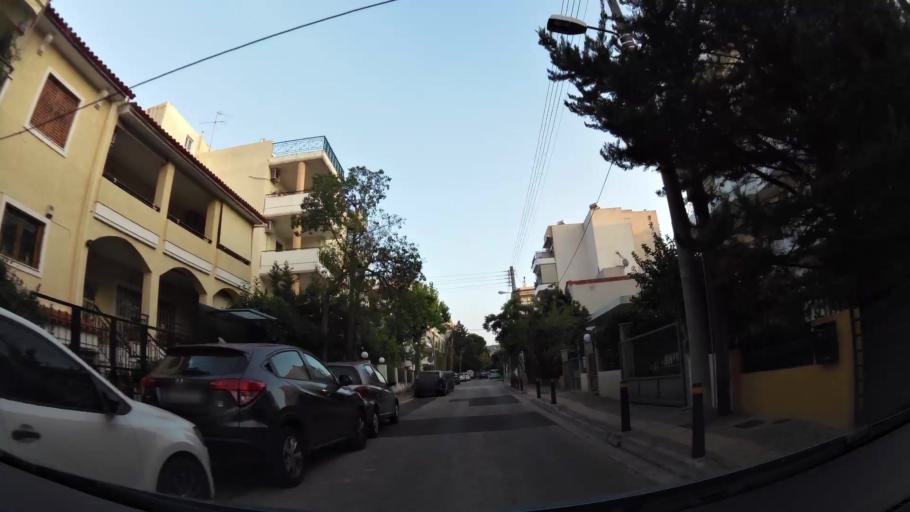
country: GR
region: Attica
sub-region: Nomarchia Athinas
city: Agia Paraskevi
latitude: 38.0170
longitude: 23.8281
